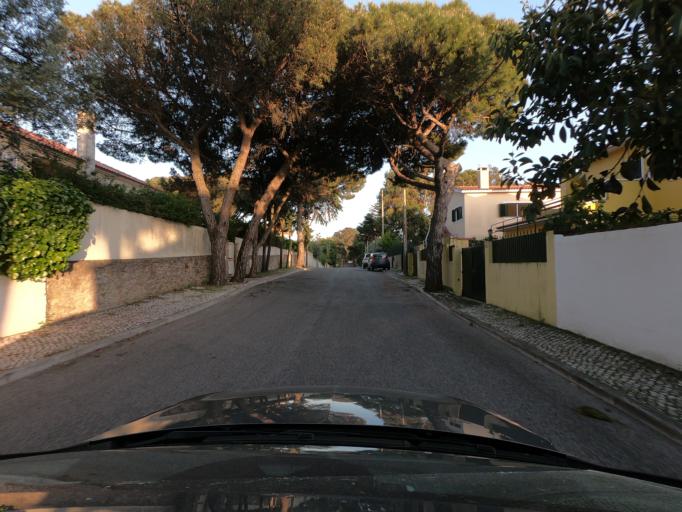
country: PT
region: Lisbon
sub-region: Sintra
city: Rio de Mouro
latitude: 38.7585
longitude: -9.3591
